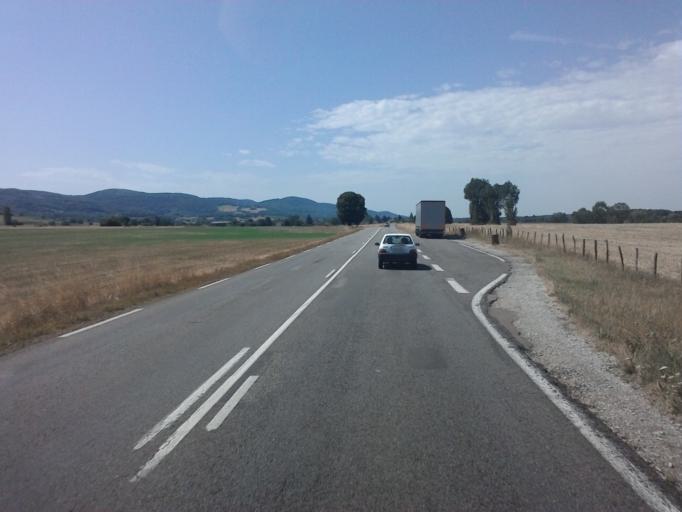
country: FR
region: Franche-Comte
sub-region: Departement du Jura
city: Montmorot
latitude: 46.6198
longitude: 5.4830
